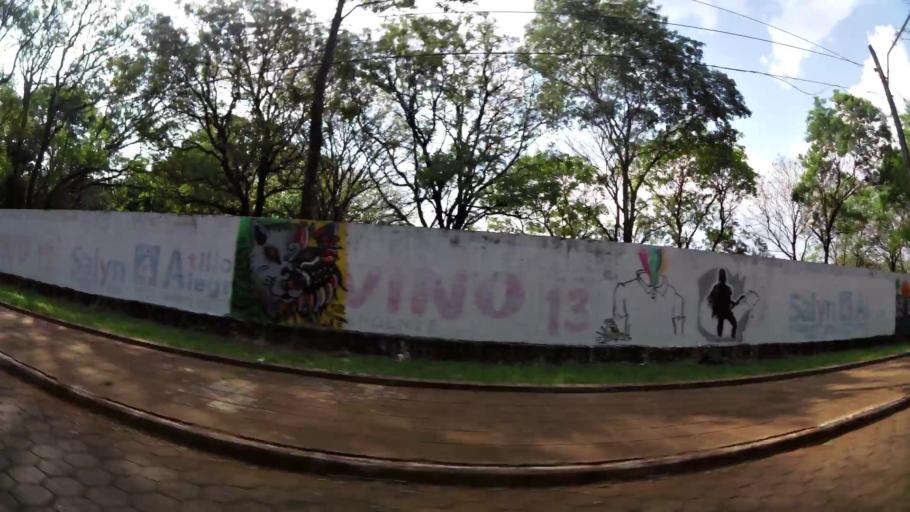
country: PY
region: Alto Parana
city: Presidente Franco
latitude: -25.5235
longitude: -54.6133
